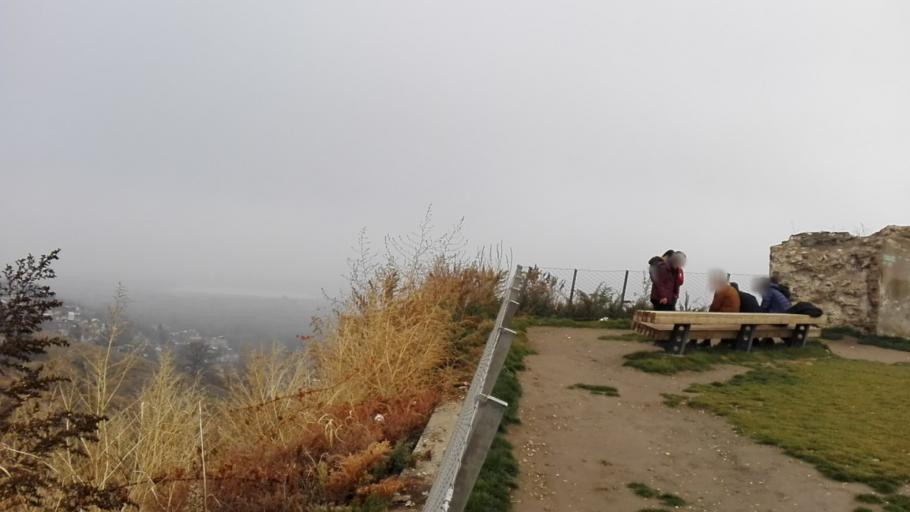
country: TR
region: Diyarbakir
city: Sur
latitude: 37.9145
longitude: 40.2434
